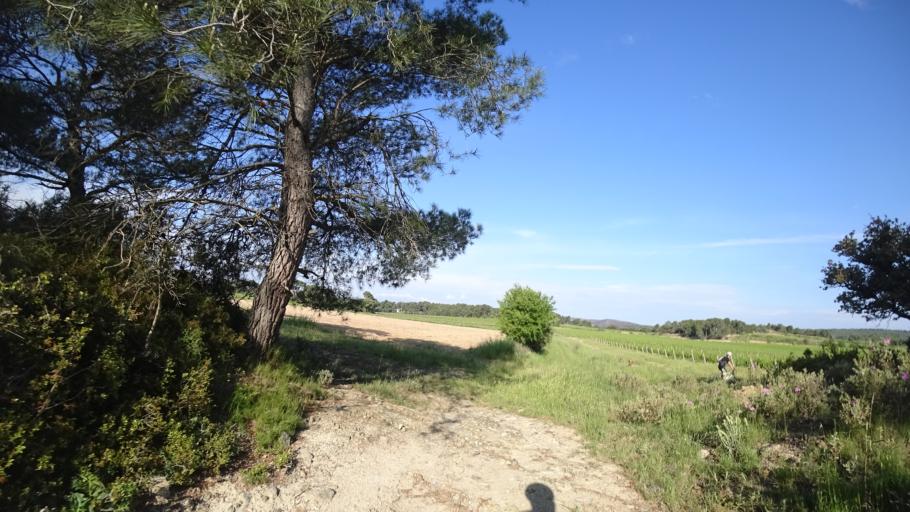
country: FR
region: Languedoc-Roussillon
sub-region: Departement de l'Aude
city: Lezignan-Corbieres
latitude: 43.2373
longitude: 2.7461
